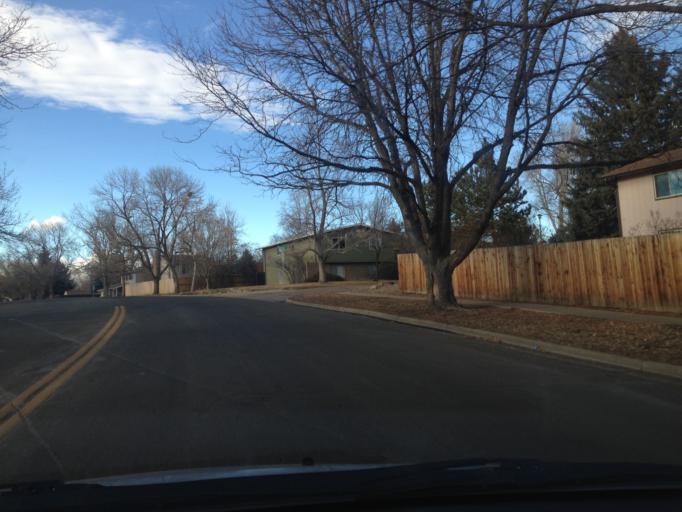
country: US
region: Colorado
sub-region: Boulder County
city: Lafayette
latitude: 39.9881
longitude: -105.1079
